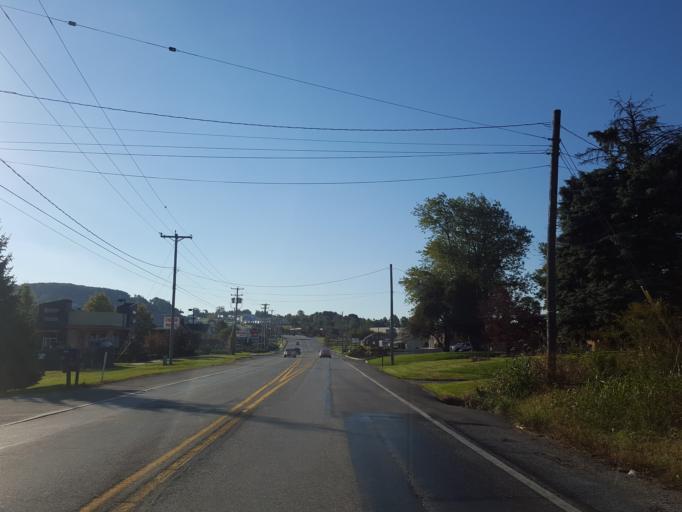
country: US
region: Pennsylvania
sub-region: York County
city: Yoe
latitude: 39.9205
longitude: -76.6328
